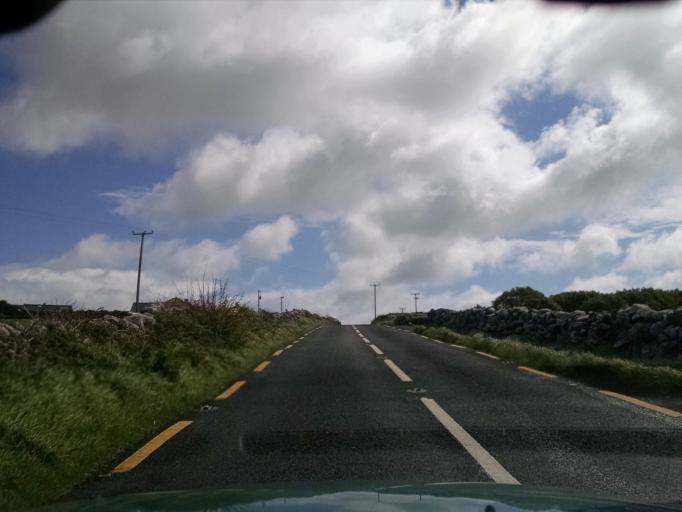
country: IE
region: Connaught
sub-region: County Galway
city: Gaillimh
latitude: 53.1500
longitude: -9.0662
